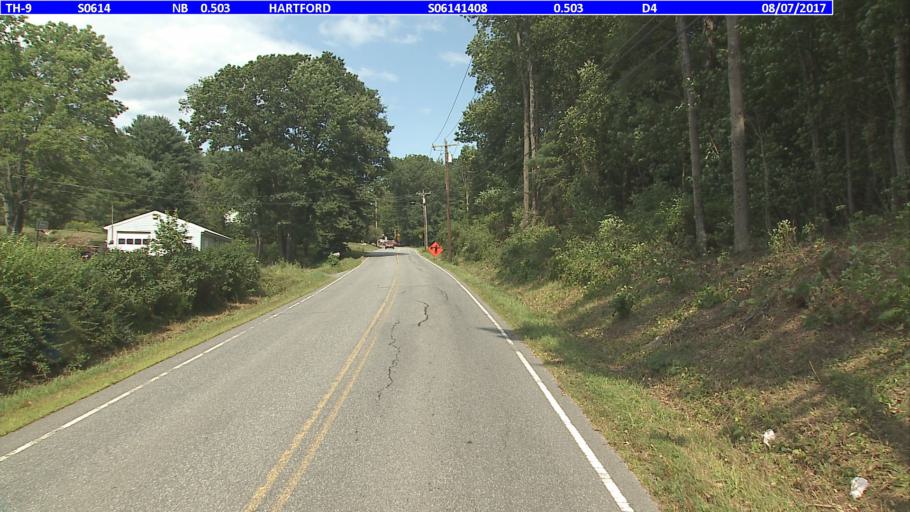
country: US
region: Vermont
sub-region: Windsor County
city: White River Junction
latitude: 43.6628
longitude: -72.3306
